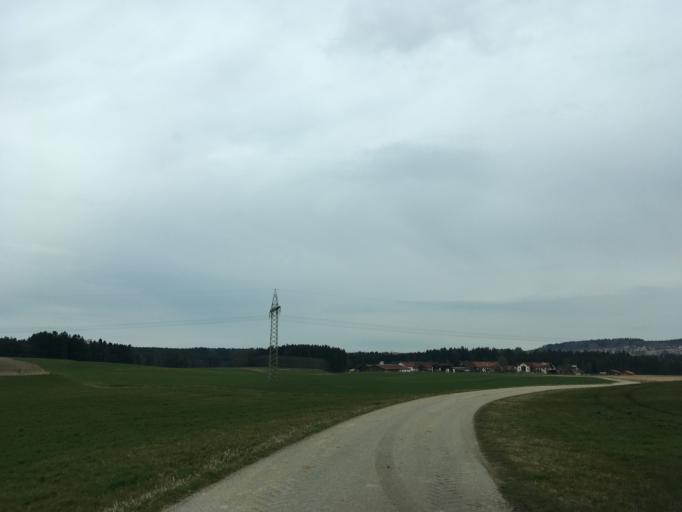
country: DE
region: Bavaria
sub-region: Upper Bavaria
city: Schnaitsee
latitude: 48.0500
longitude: 12.3773
